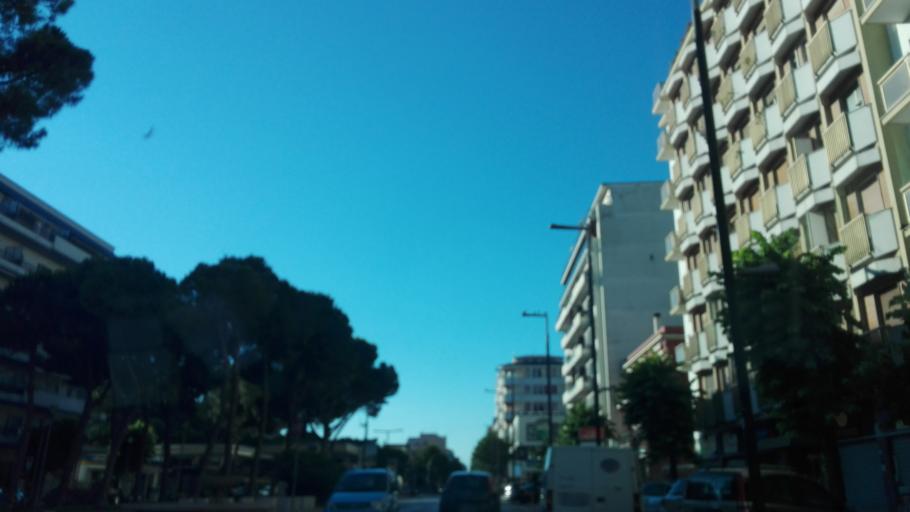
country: IT
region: Abruzzo
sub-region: Provincia di Pescara
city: Pescara
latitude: 42.4815
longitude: 14.1924
